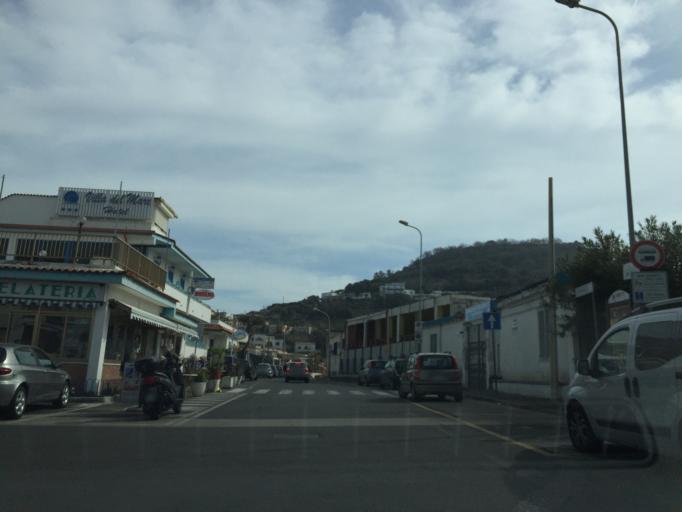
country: IT
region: Campania
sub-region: Provincia di Napoli
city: Bacoli
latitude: 40.7870
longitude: 14.0823
